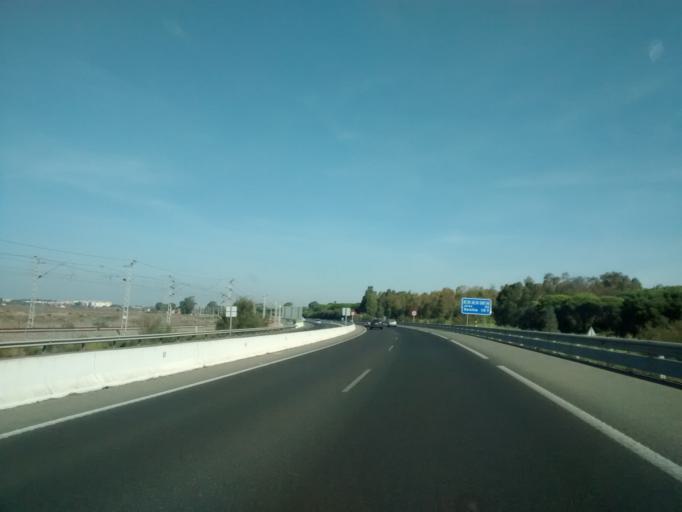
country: ES
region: Andalusia
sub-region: Provincia de Cadiz
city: Puerto Real
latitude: 36.5039
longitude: -6.1449
